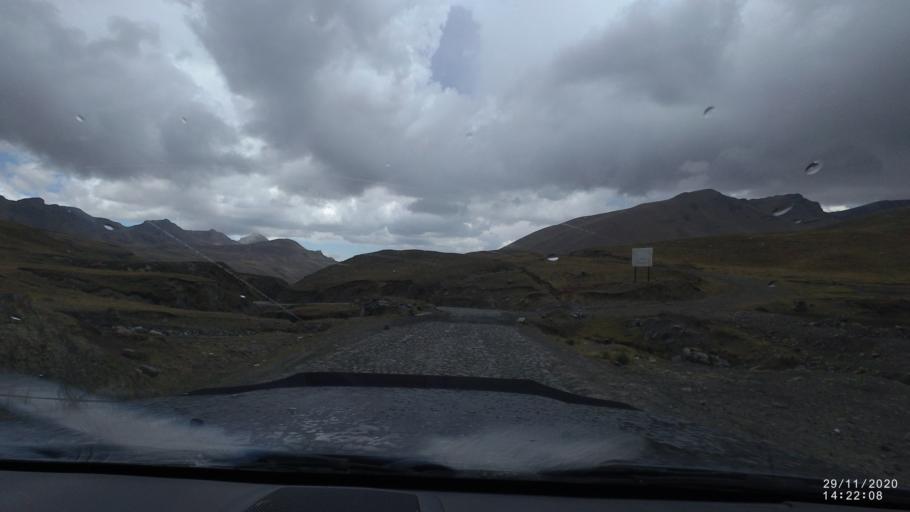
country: BO
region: Cochabamba
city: Sipe Sipe
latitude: -17.2527
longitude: -66.3899
